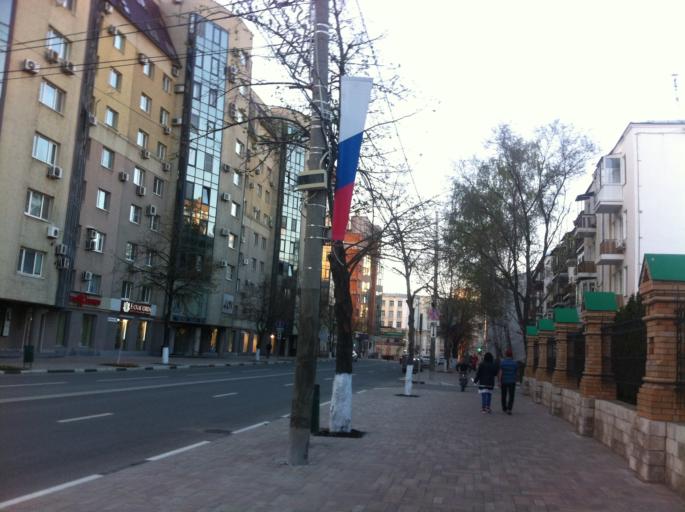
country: RU
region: Samara
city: Samara
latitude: 53.1978
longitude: 50.1039
